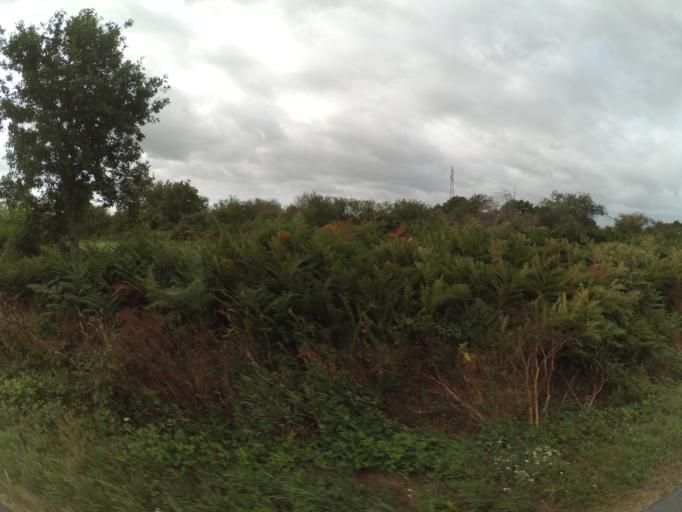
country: FR
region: Pays de la Loire
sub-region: Departement de la Loire-Atlantique
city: Getigne
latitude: 47.0785
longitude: -1.2223
